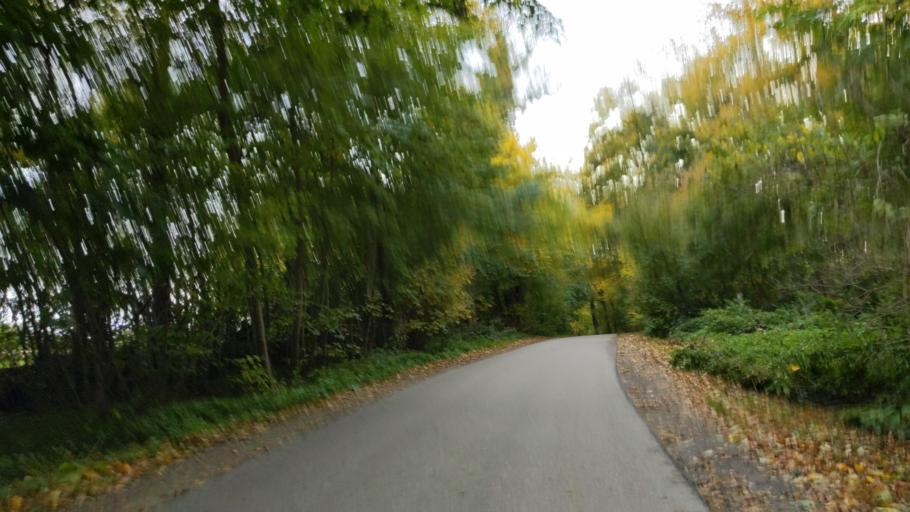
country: DE
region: Schleswig-Holstein
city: Susel
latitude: 54.1116
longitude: 10.7062
